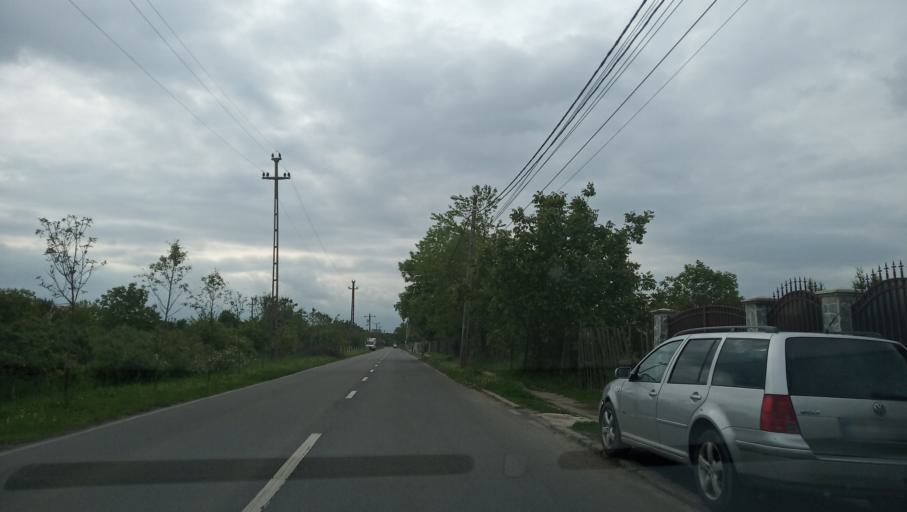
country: RO
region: Timis
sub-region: Comuna Ghiroda
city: Ghiroda
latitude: 45.7541
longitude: 21.2707
